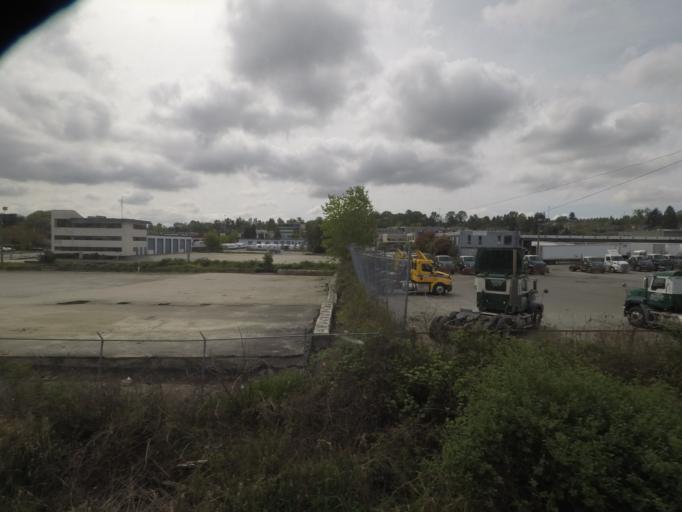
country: CA
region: British Columbia
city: Burnaby
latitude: 49.2621
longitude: -123.0155
